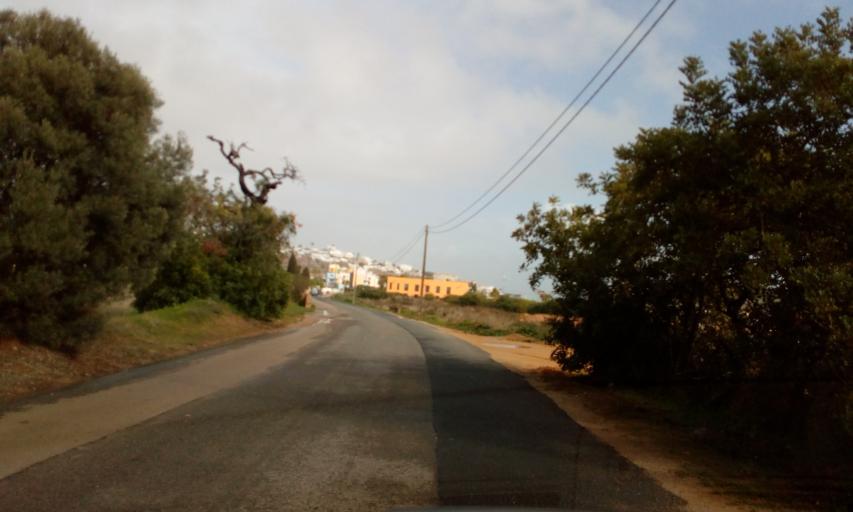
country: PT
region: Faro
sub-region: Albufeira
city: Albufeira
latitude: 37.0850
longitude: -8.2739
